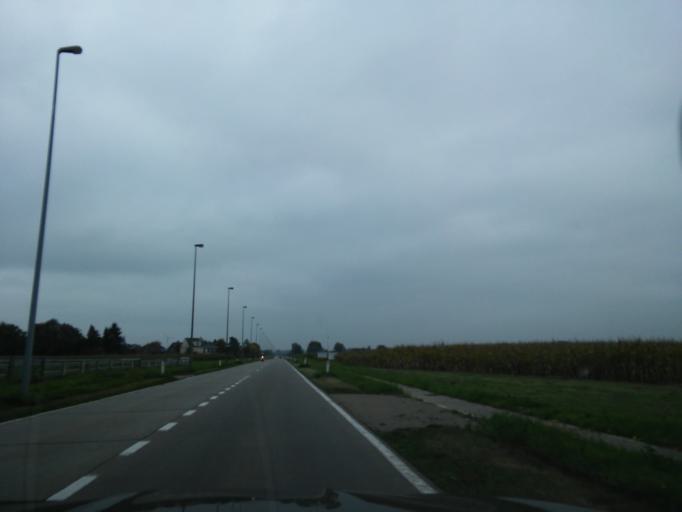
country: BE
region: Flanders
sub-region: Provincie Oost-Vlaanderen
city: Zele
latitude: 51.0566
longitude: 4.0161
